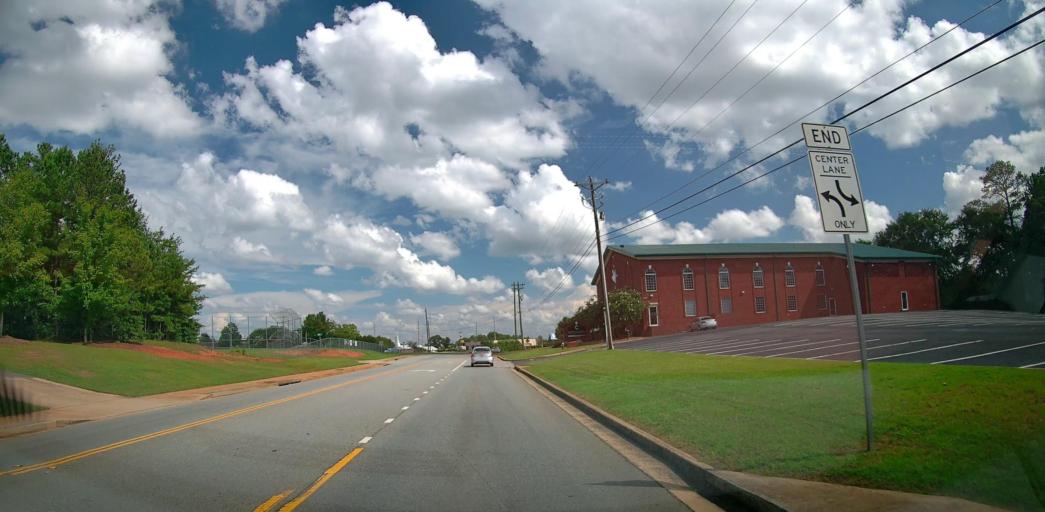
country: US
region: Georgia
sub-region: Houston County
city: Centerville
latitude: 32.5968
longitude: -83.6569
